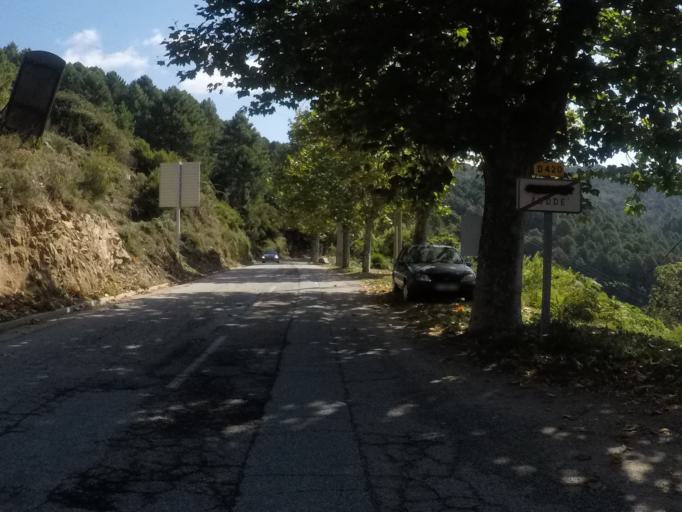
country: FR
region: Corsica
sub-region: Departement de la Corse-du-Sud
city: Zonza
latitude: 41.7688
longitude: 9.0814
